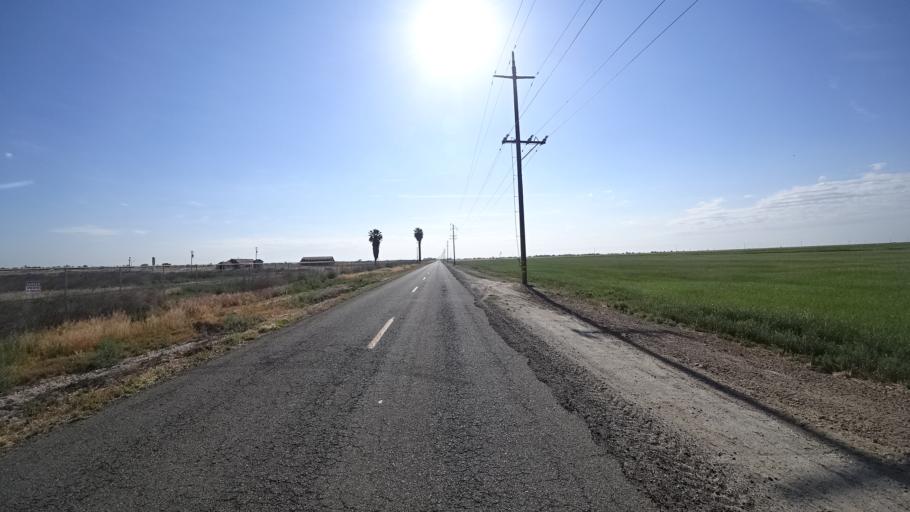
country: US
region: California
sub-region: Kings County
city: Stratford
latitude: 36.2257
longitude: -119.7561
